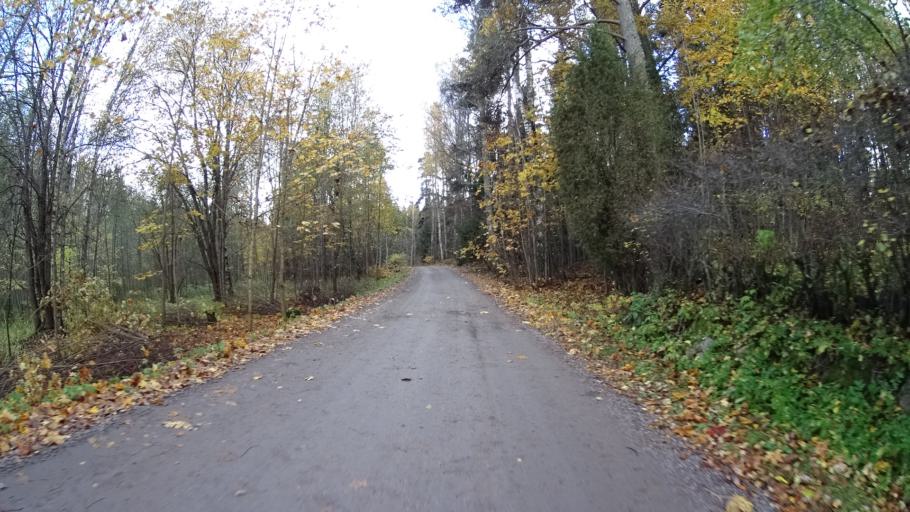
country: FI
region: Uusimaa
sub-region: Helsinki
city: Kilo
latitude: 60.2593
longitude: 24.7912
